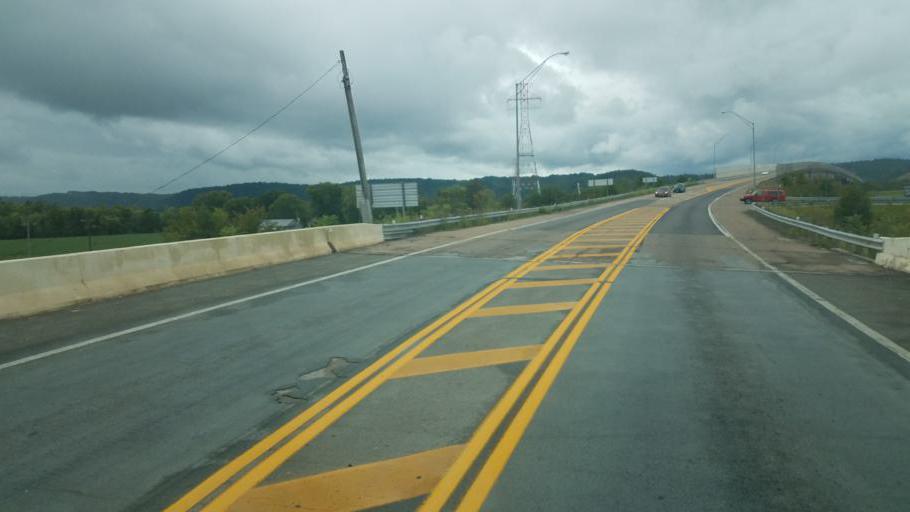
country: US
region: Ohio
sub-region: Scioto County
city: Franklin Furnace
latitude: 38.6477
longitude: -82.8518
